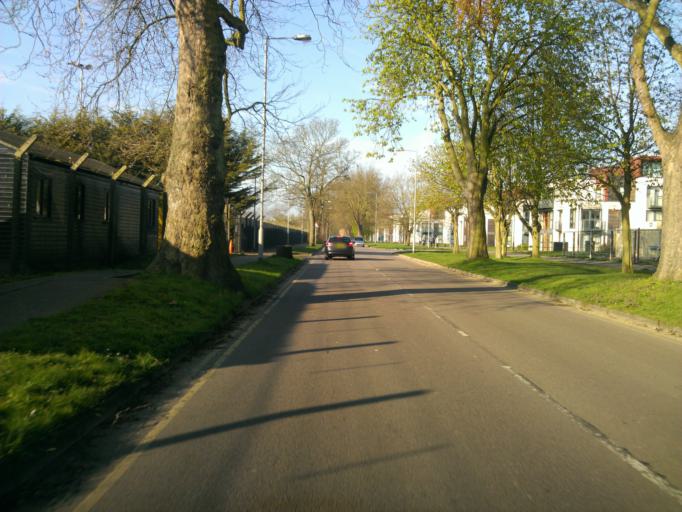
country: GB
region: England
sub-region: Essex
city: Colchester
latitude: 51.8829
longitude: 0.8964
